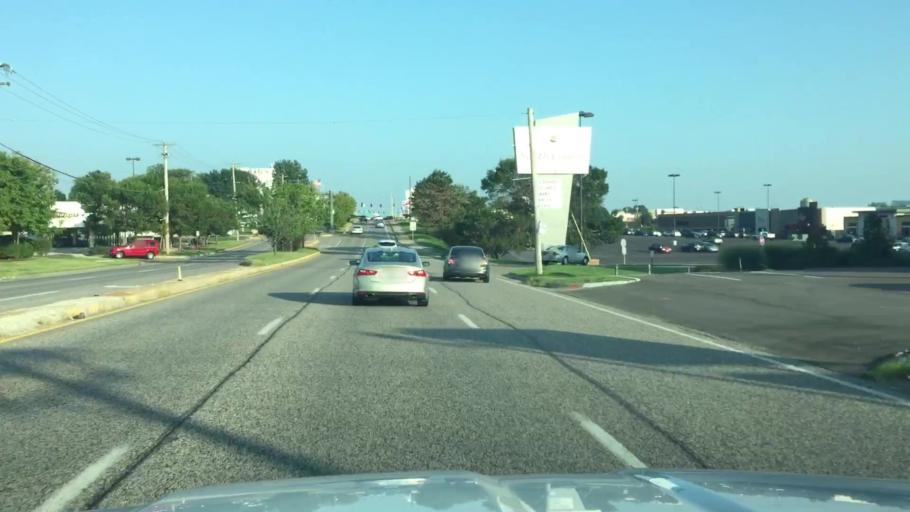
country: US
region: Missouri
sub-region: Saint Louis County
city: Mehlville
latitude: 38.5093
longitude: -90.3319
